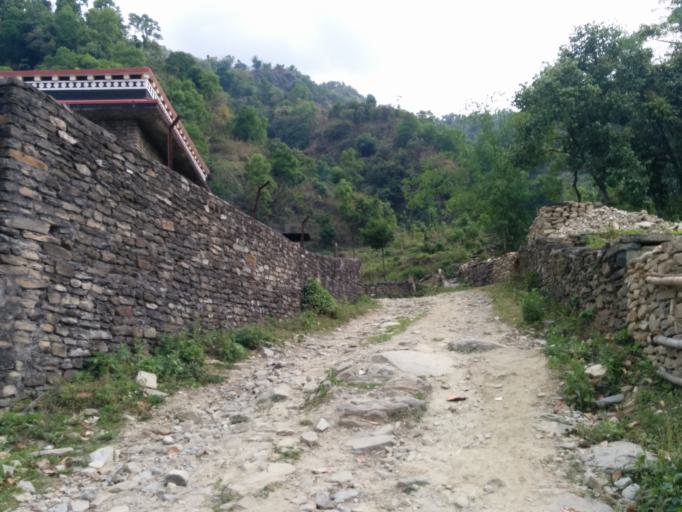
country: NP
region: Western Region
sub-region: Gandaki Zone
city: Pokhara
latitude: 28.2305
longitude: 83.9490
